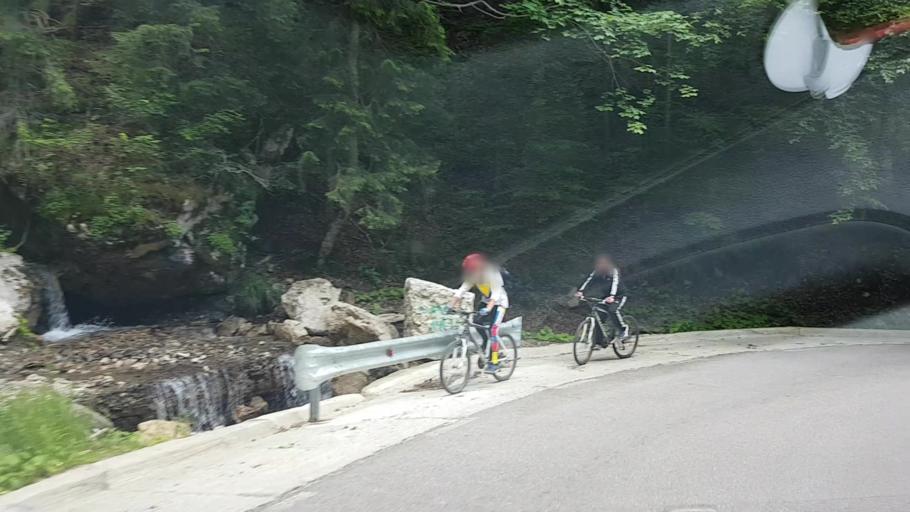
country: RO
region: Suceava
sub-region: Comuna Crucea
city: Crucea
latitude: 47.4356
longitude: 25.5720
